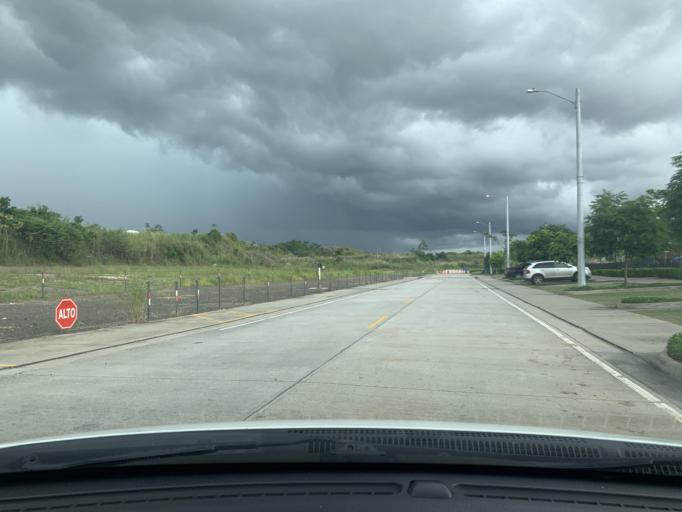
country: PA
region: Panama
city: San Miguelito
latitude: 9.0929
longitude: -79.4694
